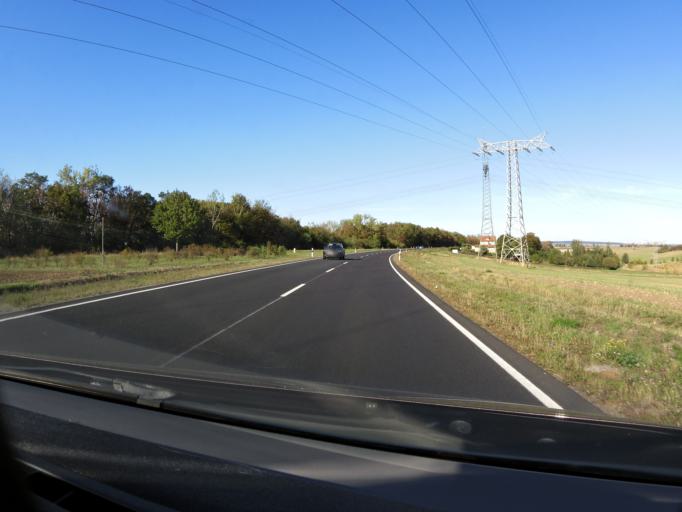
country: DE
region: Saxony-Anhalt
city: Quedlinburg
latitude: 51.7982
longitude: 11.1857
